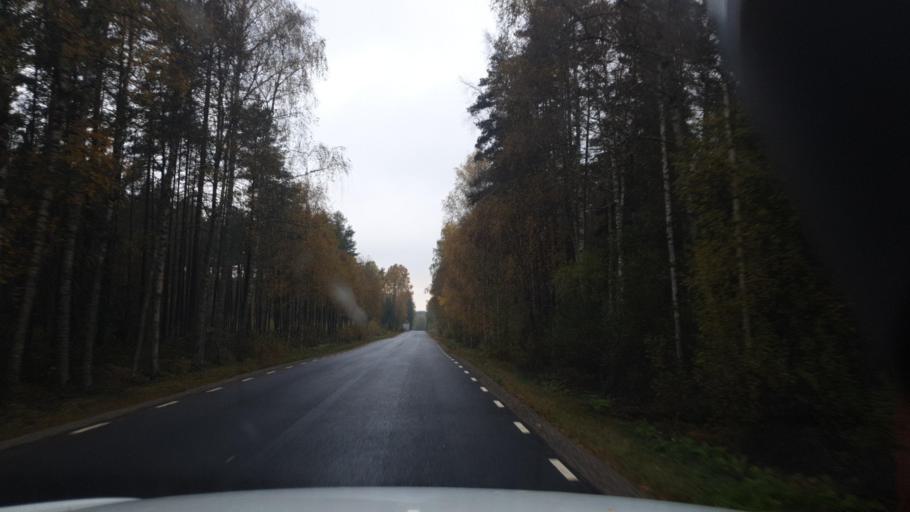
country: SE
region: Vaermland
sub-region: Arvika Kommun
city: Arvika
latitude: 59.6548
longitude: 12.7286
